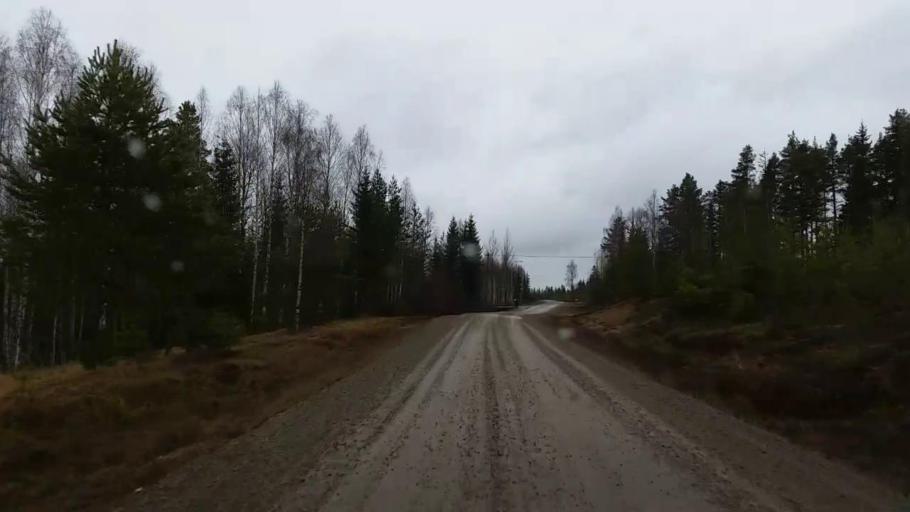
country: SE
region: Gaevleborg
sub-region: Ljusdals Kommun
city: Farila
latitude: 62.1314
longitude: 15.6629
